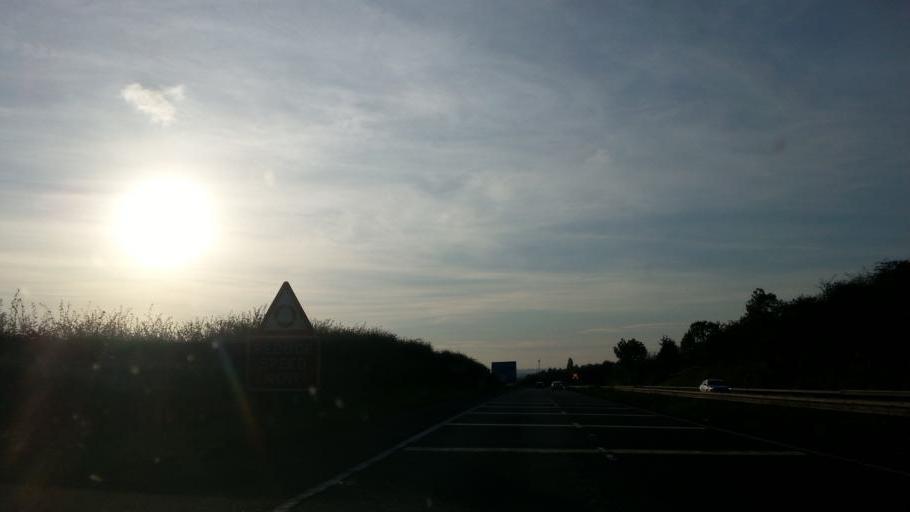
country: GB
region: England
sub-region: Herefordshire
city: Ross on Wye
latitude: 51.9291
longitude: -2.5554
